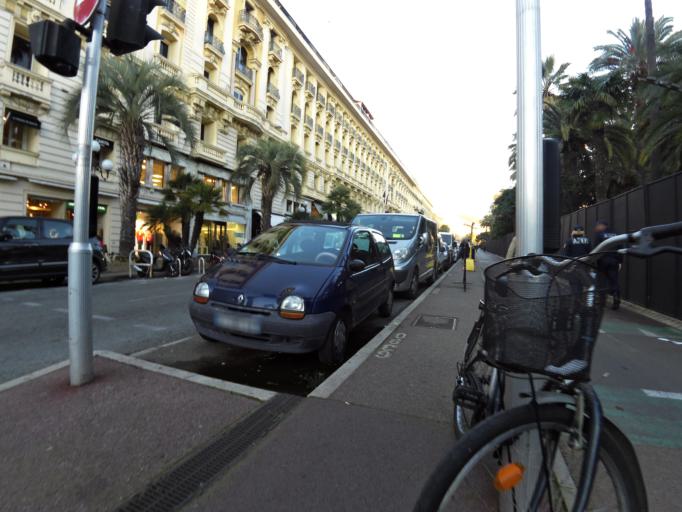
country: FR
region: Provence-Alpes-Cote d'Azur
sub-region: Departement des Alpes-Maritimes
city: Nice
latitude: 43.6964
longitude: 7.2678
